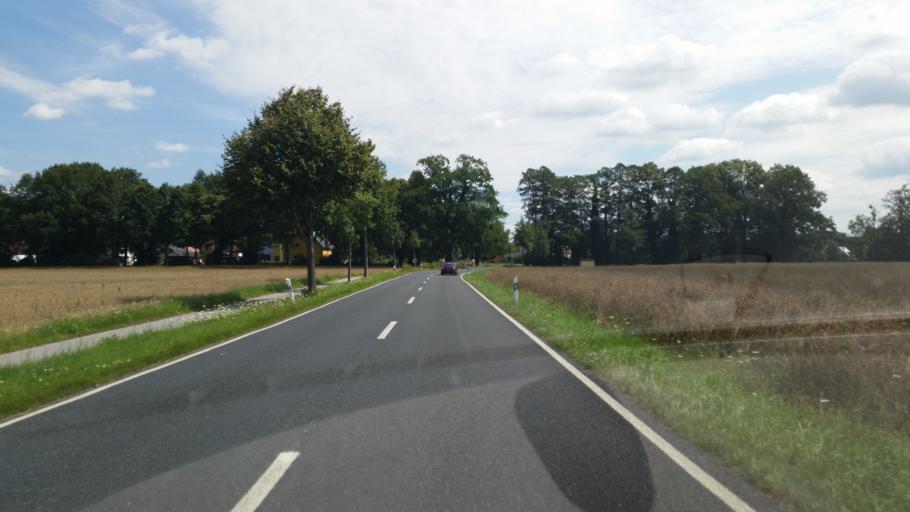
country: DE
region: Saxony
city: Nebelschutz
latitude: 51.2859
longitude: 14.1402
